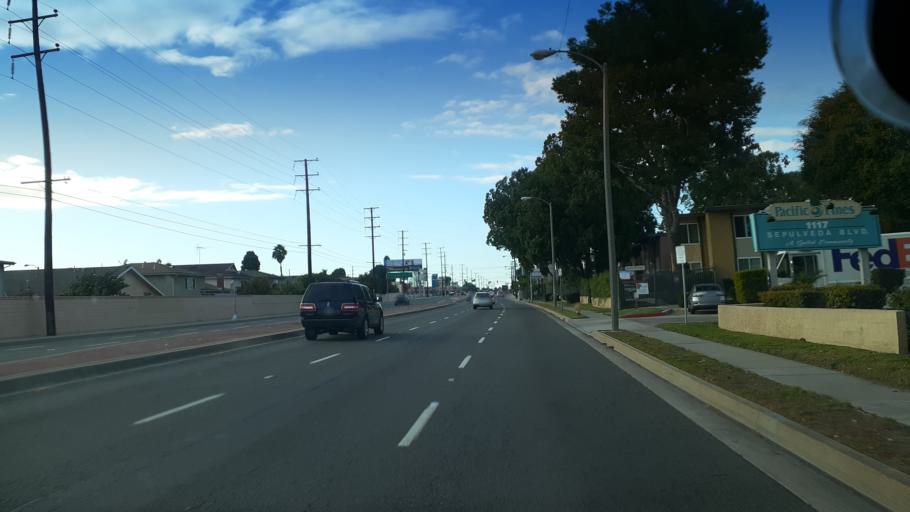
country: US
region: California
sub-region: Los Angeles County
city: West Carson
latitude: 33.8119
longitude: -118.2943
